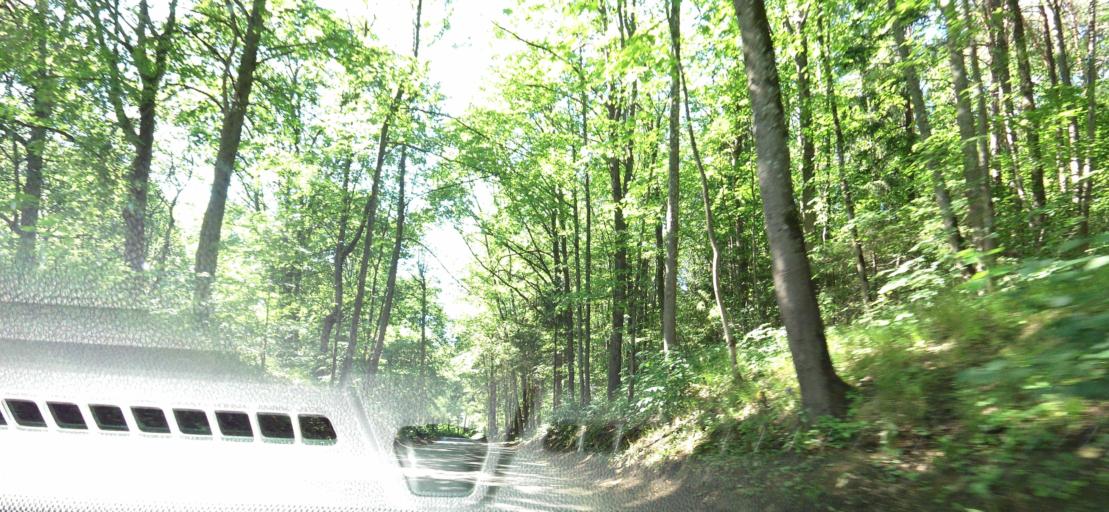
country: LT
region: Vilnius County
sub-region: Vilnius
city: Fabijoniskes
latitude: 54.7491
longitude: 25.3006
